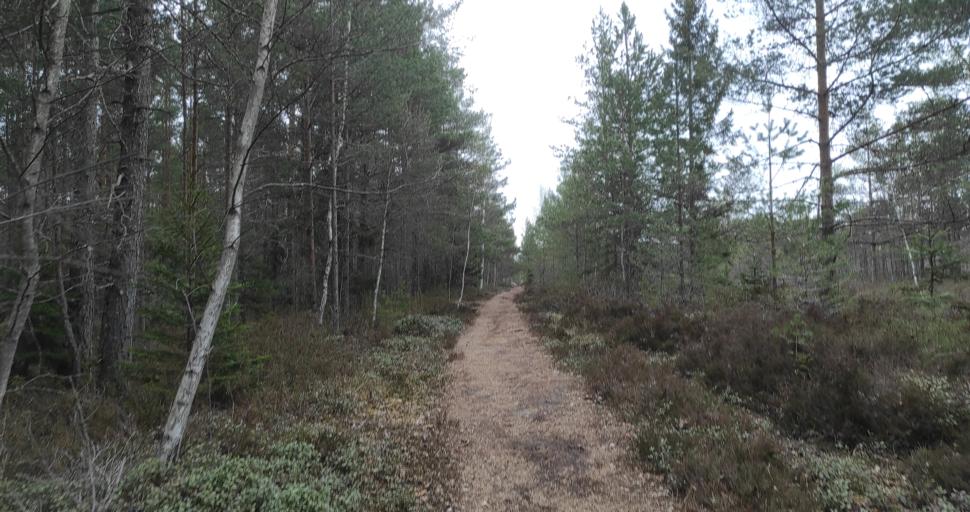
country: LV
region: Dundaga
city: Dundaga
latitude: 57.3465
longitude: 22.1498
